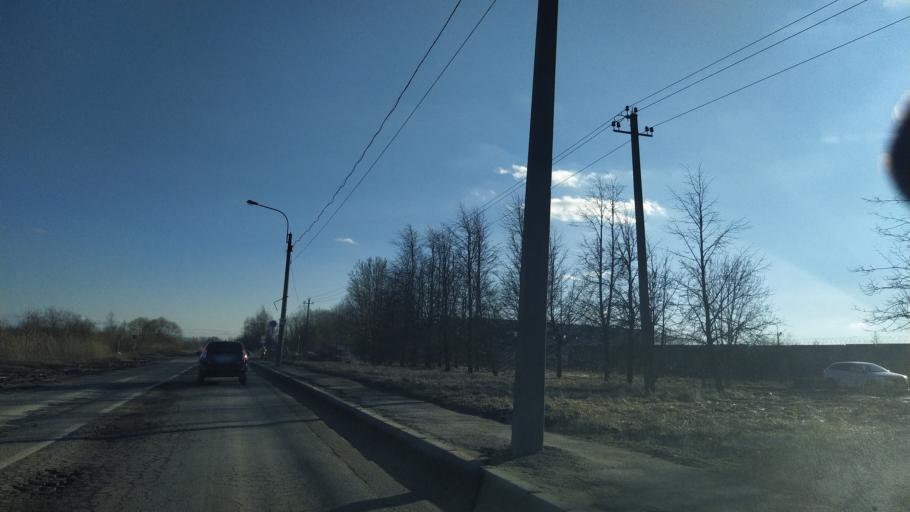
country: RU
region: St.-Petersburg
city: Pushkin
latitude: 59.6961
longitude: 30.3955
